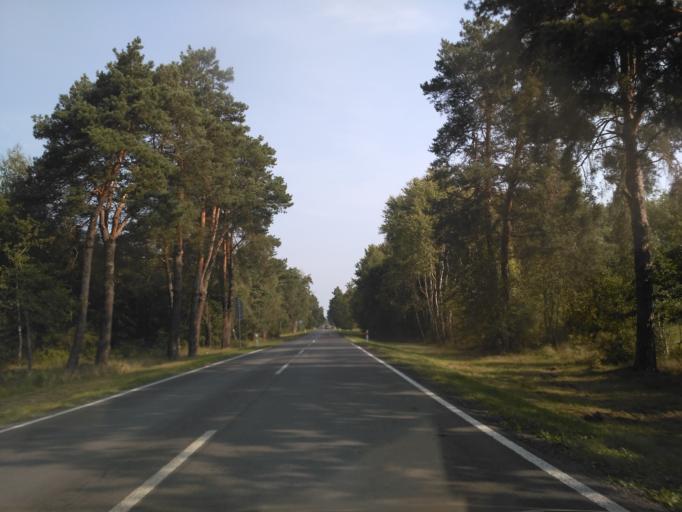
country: PL
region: Lublin Voivodeship
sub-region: Powiat leczynski
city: Cycow
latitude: 51.3368
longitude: 23.1554
